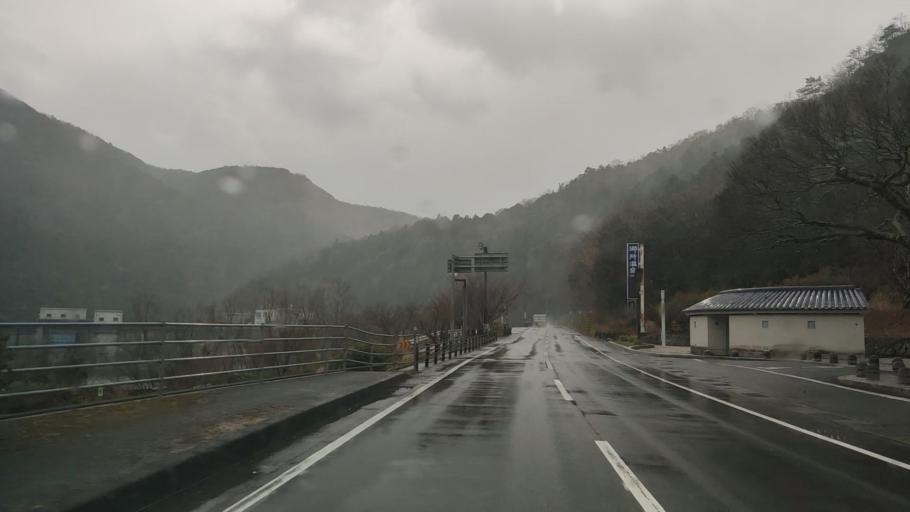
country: JP
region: Tokushima
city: Kamojimacho-jogejima
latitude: 34.1500
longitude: 134.3528
